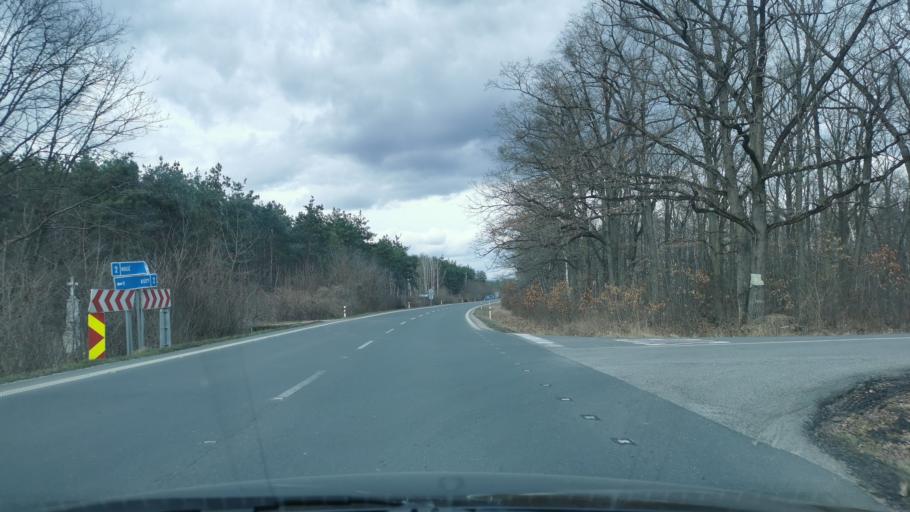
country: CZ
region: South Moravian
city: Tynec
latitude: 48.7290
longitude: 17.0480
